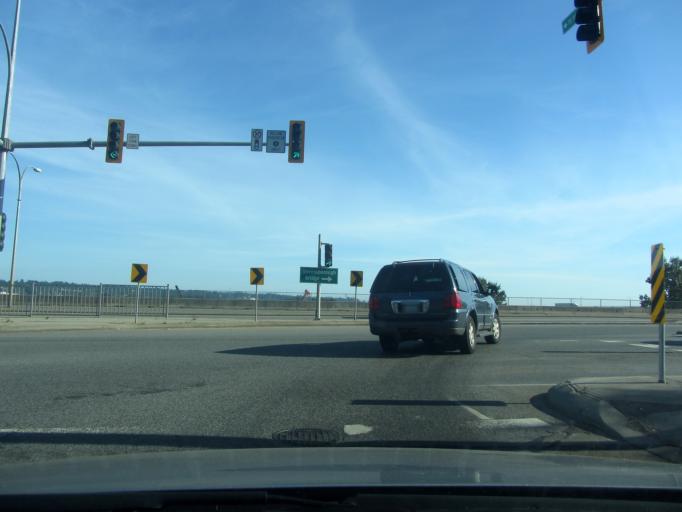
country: CA
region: British Columbia
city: New Westminster
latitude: 49.2001
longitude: -122.9455
